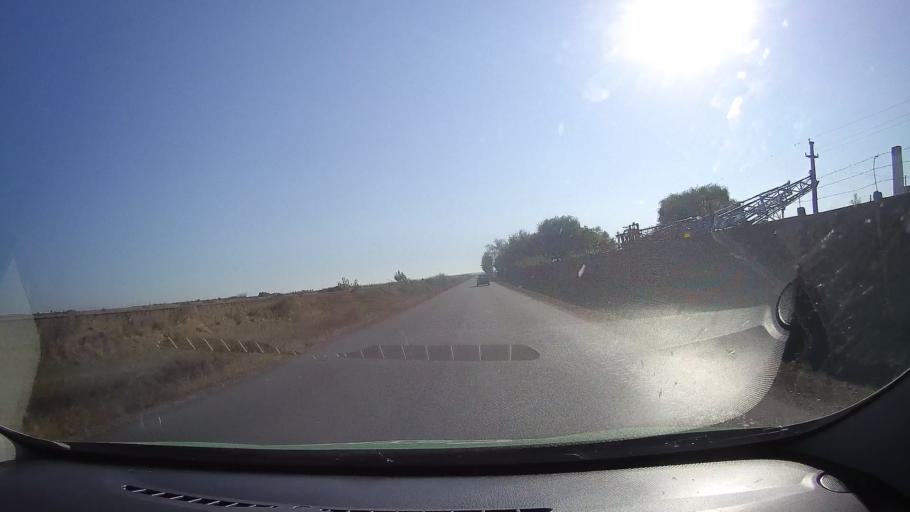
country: RO
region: Satu Mare
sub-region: Comuna Santau
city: Santau
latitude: 47.5070
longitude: 22.5268
